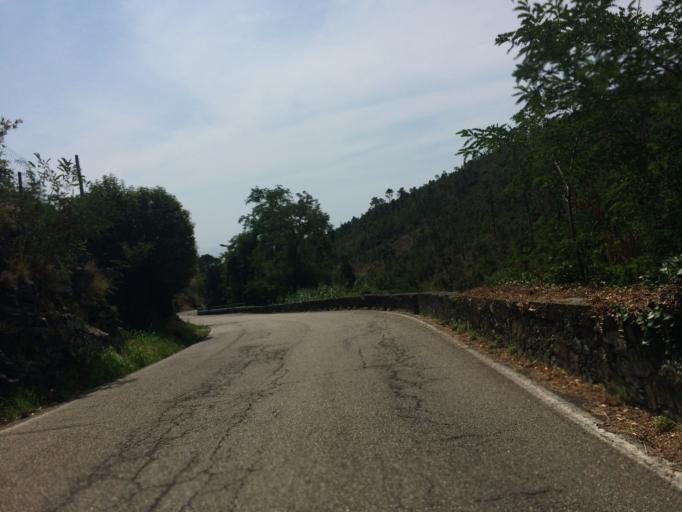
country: IT
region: Liguria
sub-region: Provincia di Genova
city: Cogoleto
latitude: 44.3905
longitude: 8.6293
